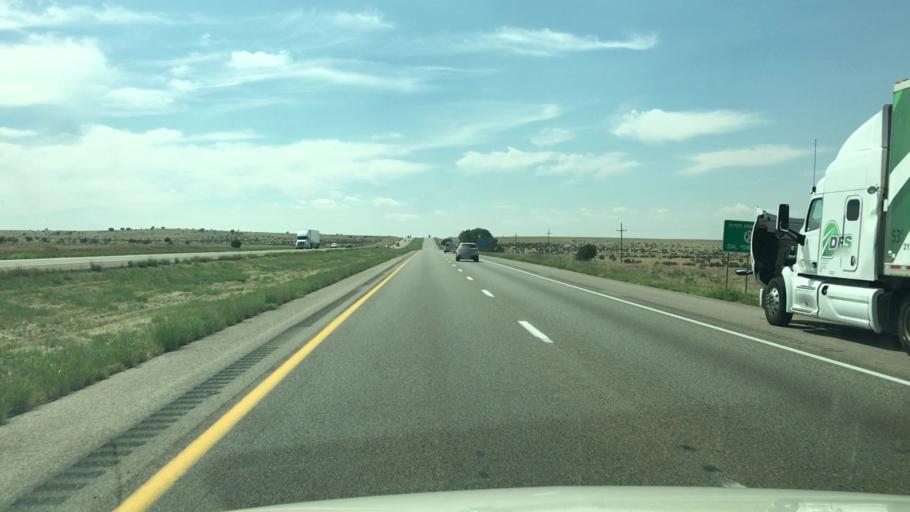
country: US
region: New Mexico
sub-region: Guadalupe County
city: Santa Rosa
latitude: 34.9788
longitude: -105.0356
